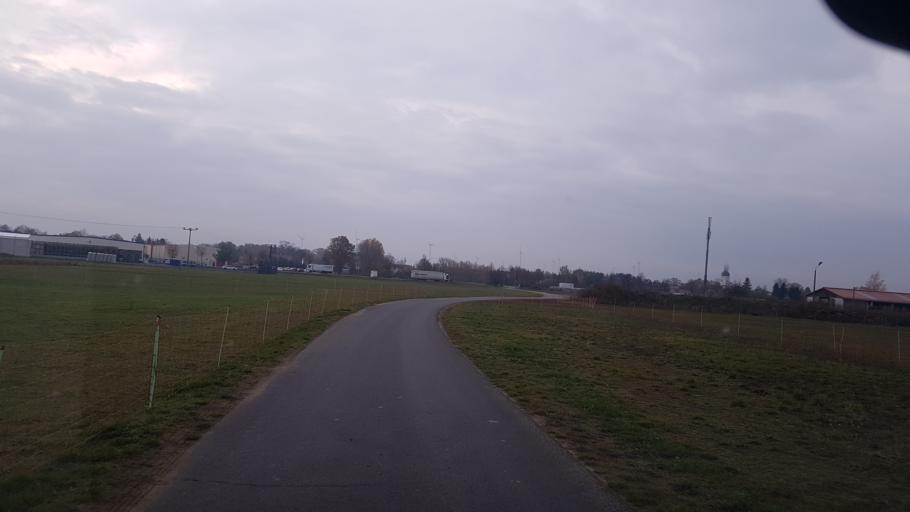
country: DE
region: Brandenburg
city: Falkenberg
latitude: 51.6014
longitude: 13.3009
